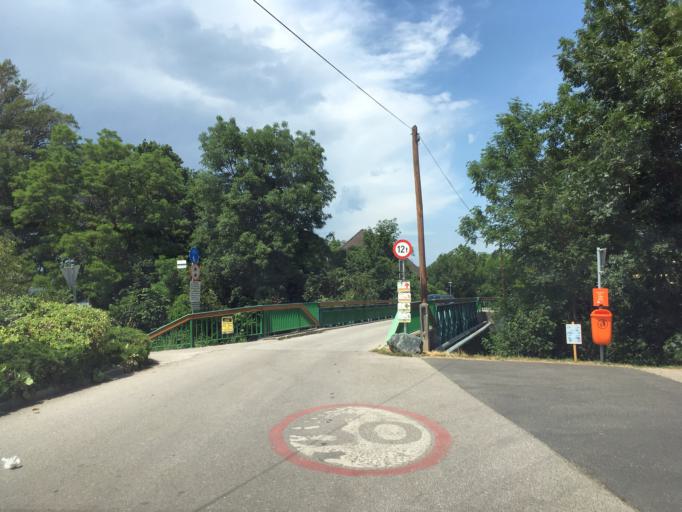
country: AT
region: Lower Austria
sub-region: Politischer Bezirk Baden
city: Teesdorf
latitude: 47.9492
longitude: 16.2757
